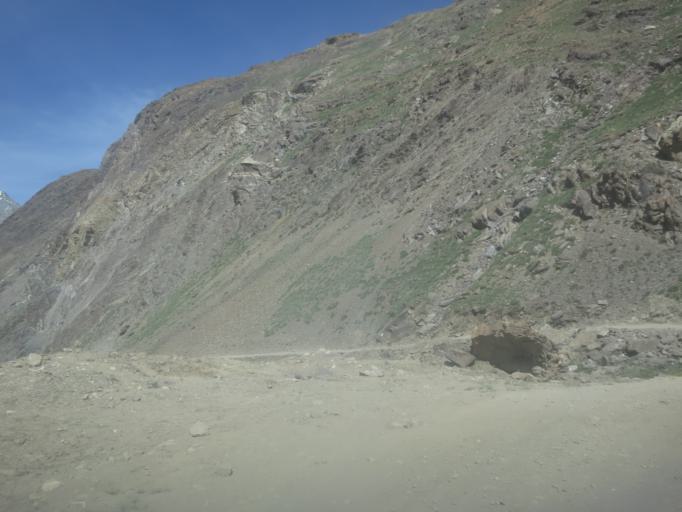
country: IN
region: Himachal Pradesh
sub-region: Kulu
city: Manali
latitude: 32.4373
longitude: 77.6816
